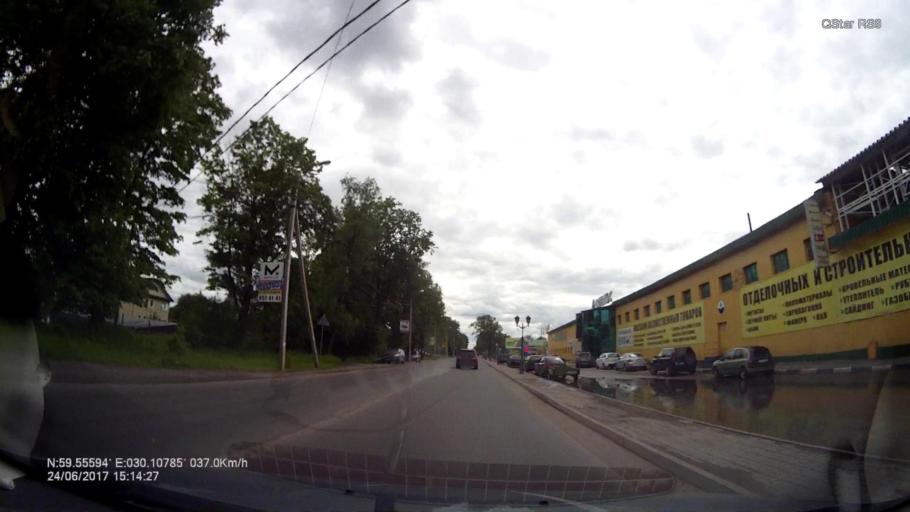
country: RU
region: Leningrad
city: Gatchina
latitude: 59.5557
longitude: 30.1076
